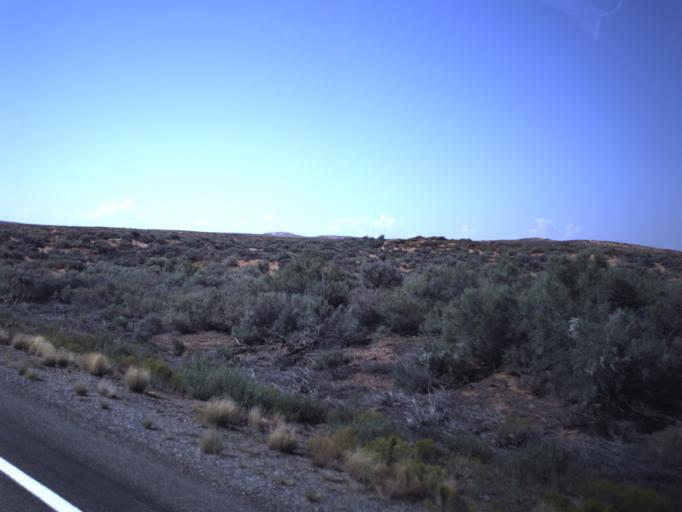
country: US
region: Utah
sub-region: San Juan County
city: Blanding
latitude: 37.0966
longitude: -109.5477
